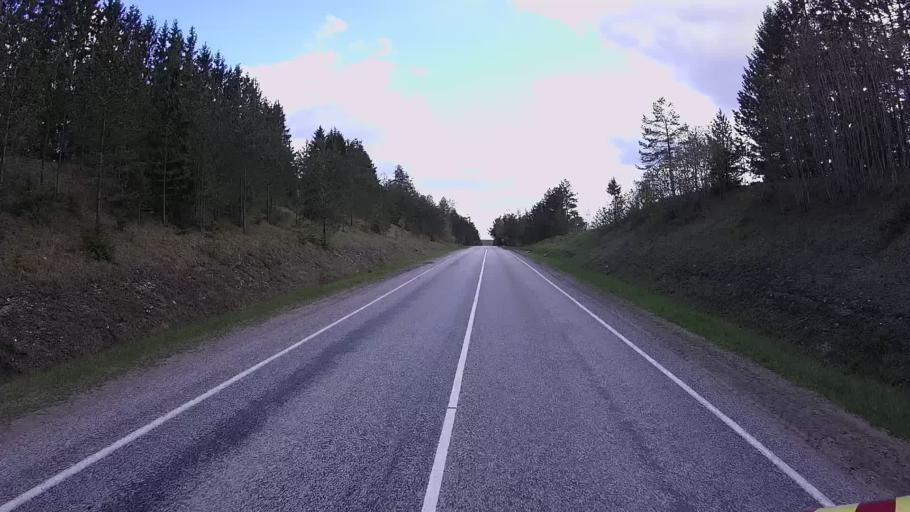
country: EE
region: Jogevamaa
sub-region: Jogeva linn
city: Jogeva
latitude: 58.7842
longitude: 26.4758
